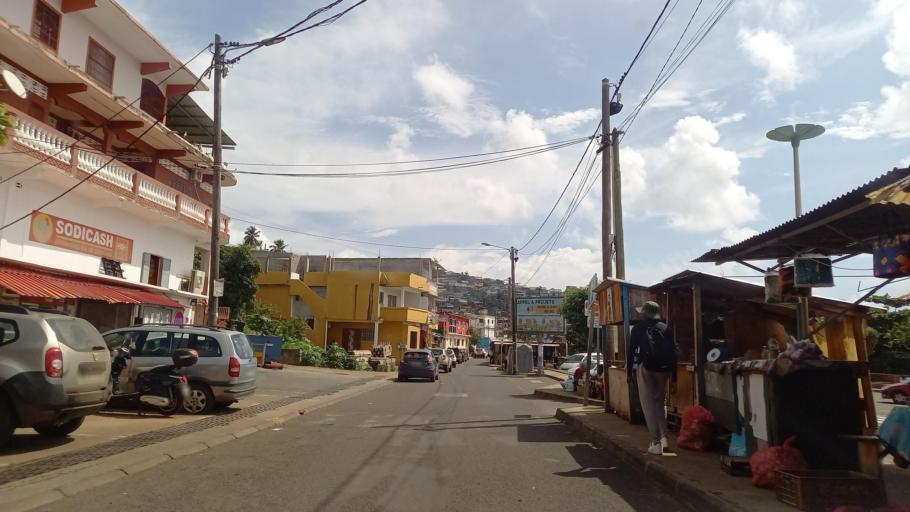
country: YT
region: Sada
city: Sada
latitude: -12.8475
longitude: 45.1008
